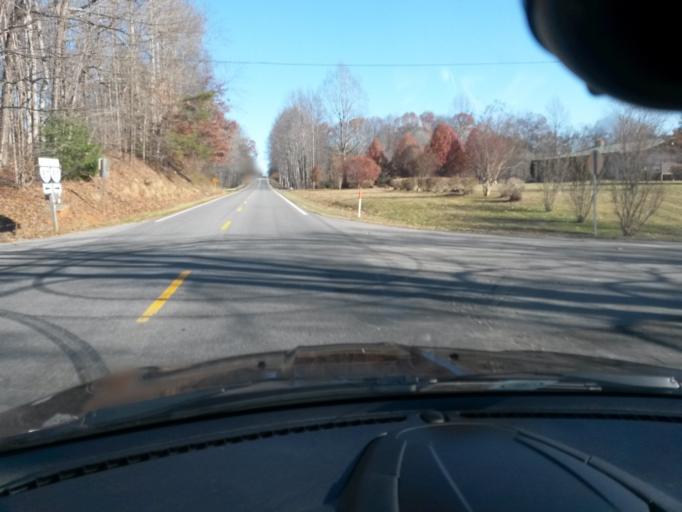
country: US
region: Virginia
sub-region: Patrick County
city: Patrick Springs
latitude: 36.7598
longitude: -80.1787
